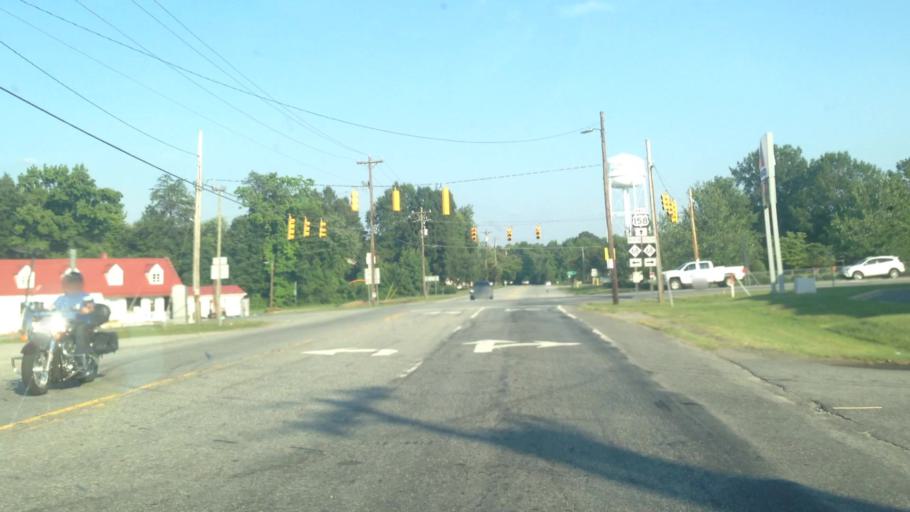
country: US
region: North Carolina
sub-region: Guilford County
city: Stokesdale
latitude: 36.2377
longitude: -79.9799
